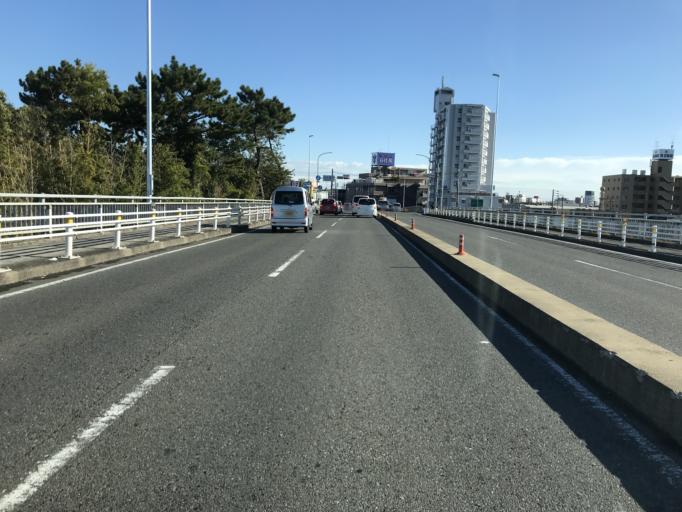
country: JP
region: Aichi
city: Nagoya-shi
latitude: 35.1790
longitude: 136.8468
